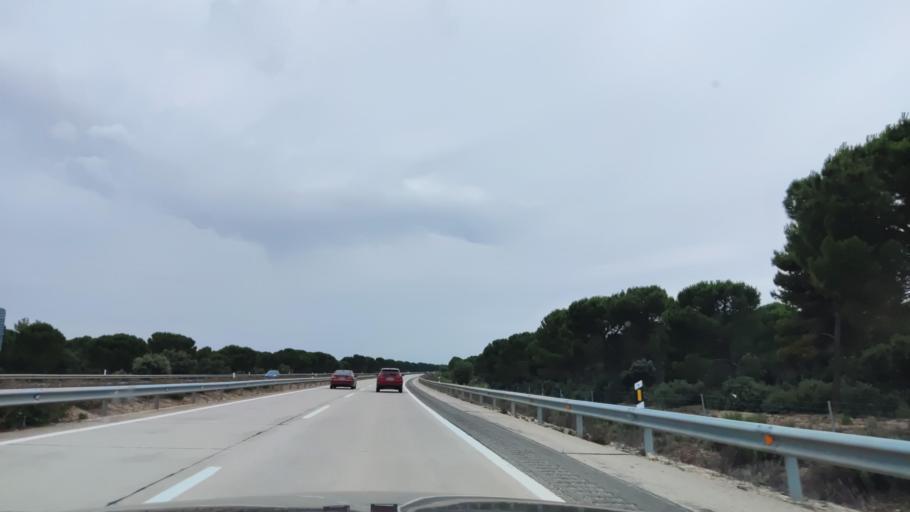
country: ES
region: Castille-La Mancha
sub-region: Provincia de Cuenca
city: Pozoamargo
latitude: 39.3465
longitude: -2.2000
